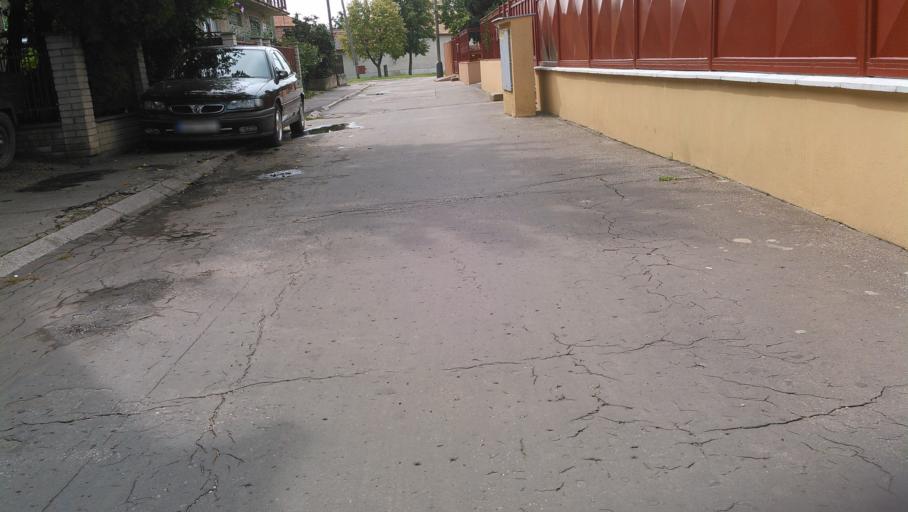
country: SK
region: Nitriansky
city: Kolarovo
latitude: 47.9117
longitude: 17.9924
